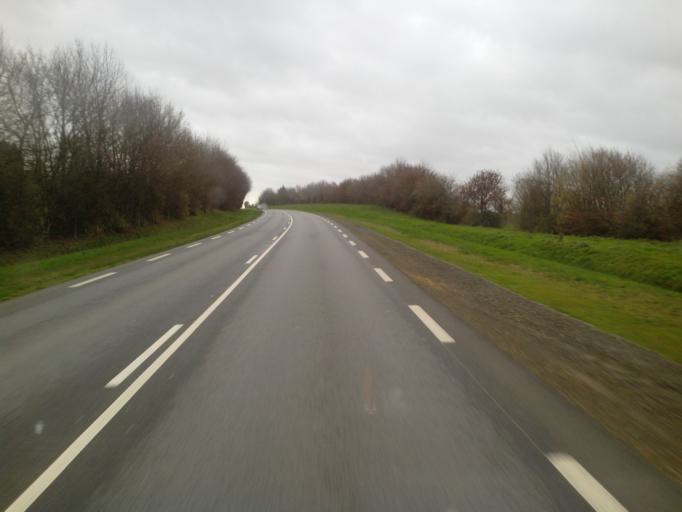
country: FR
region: Brittany
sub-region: Departement d'Ille-et-Vilaine
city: Chevaigne
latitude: 48.2406
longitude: -1.6218
